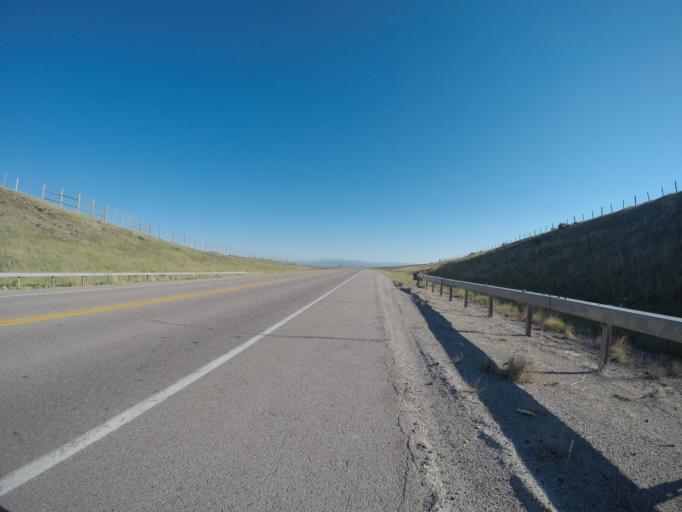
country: US
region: Wyoming
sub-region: Sublette County
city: Pinedale
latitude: 42.9134
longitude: -110.0784
